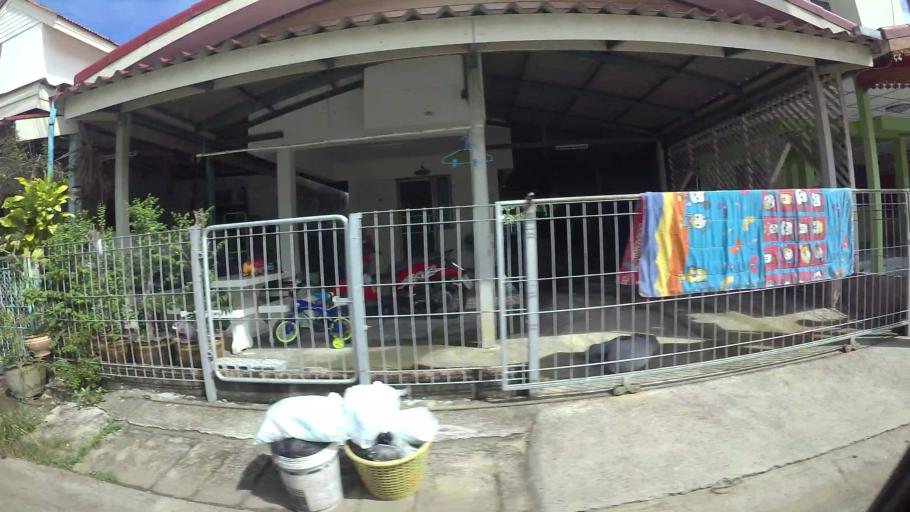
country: TH
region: Chon Buri
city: Sattahip
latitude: 12.6701
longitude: 100.9563
